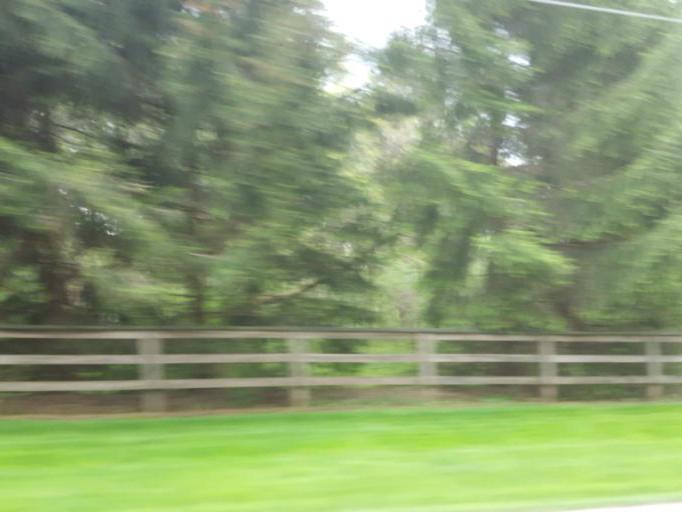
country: US
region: Ohio
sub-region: Richland County
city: Ontario
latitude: 40.7470
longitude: -82.5599
